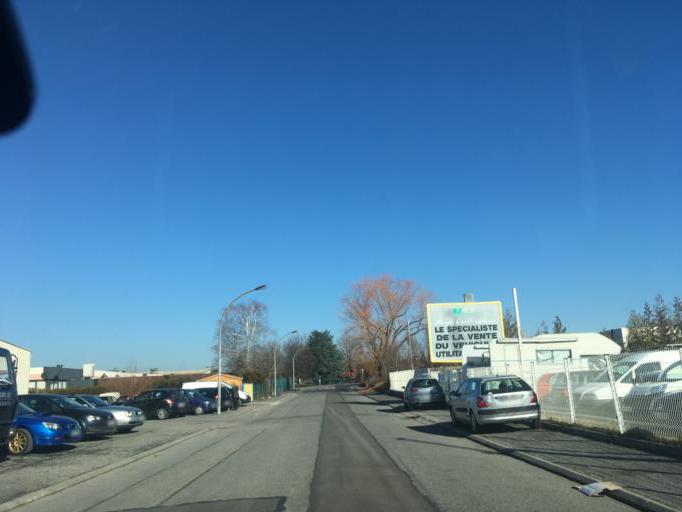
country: FR
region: Rhone-Alpes
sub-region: Departement de la Haute-Savoie
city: Ville-la-Grand
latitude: 46.1972
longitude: 6.2603
